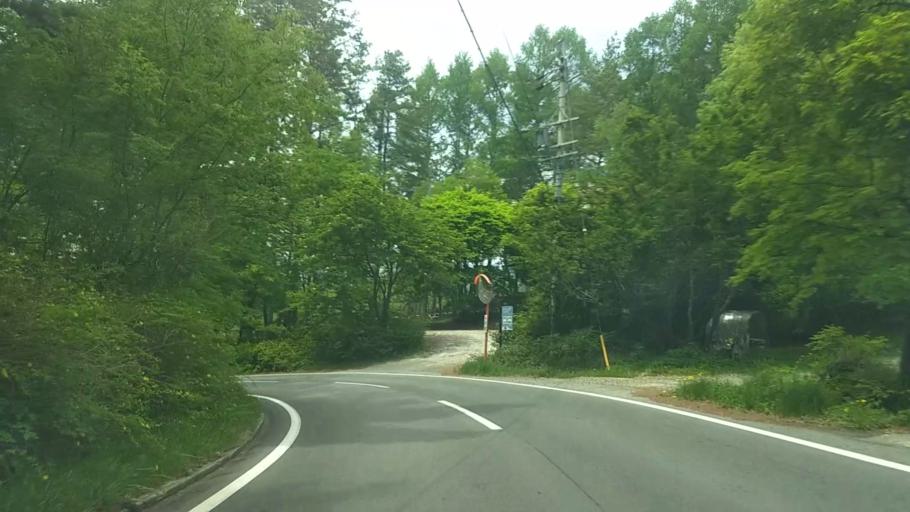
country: JP
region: Nagano
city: Chino
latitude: 36.0351
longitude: 138.2642
